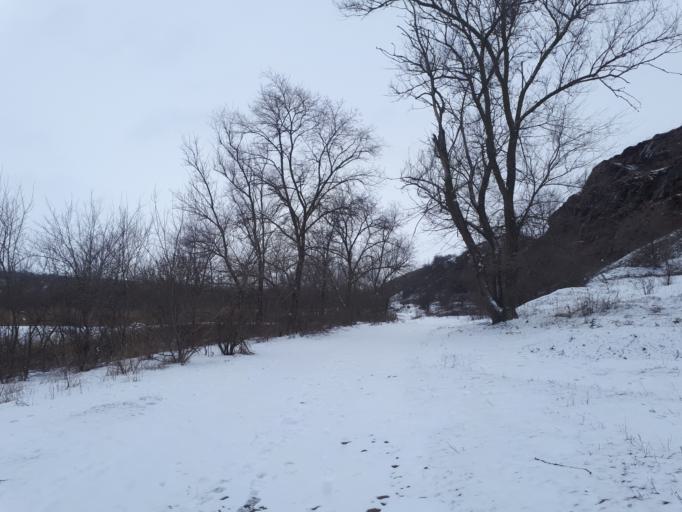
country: RU
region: Rostov
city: Krasnyy Sulin
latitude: 47.9051
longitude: 40.0459
